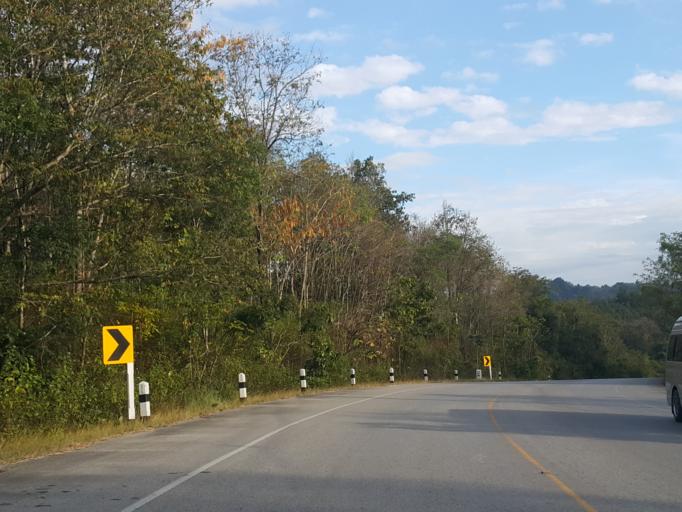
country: TH
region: Lampang
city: Chae Hom
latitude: 18.5579
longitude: 99.5589
